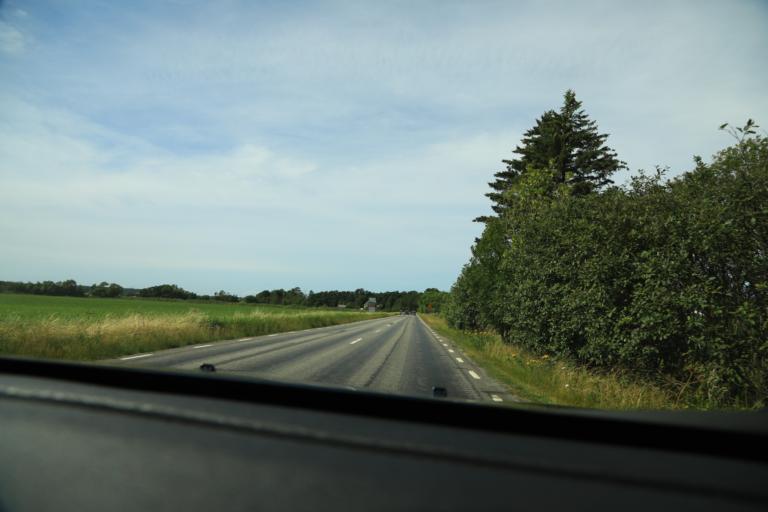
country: SE
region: Halland
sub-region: Varbergs Kommun
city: Varberg
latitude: 57.1432
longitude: 12.2798
